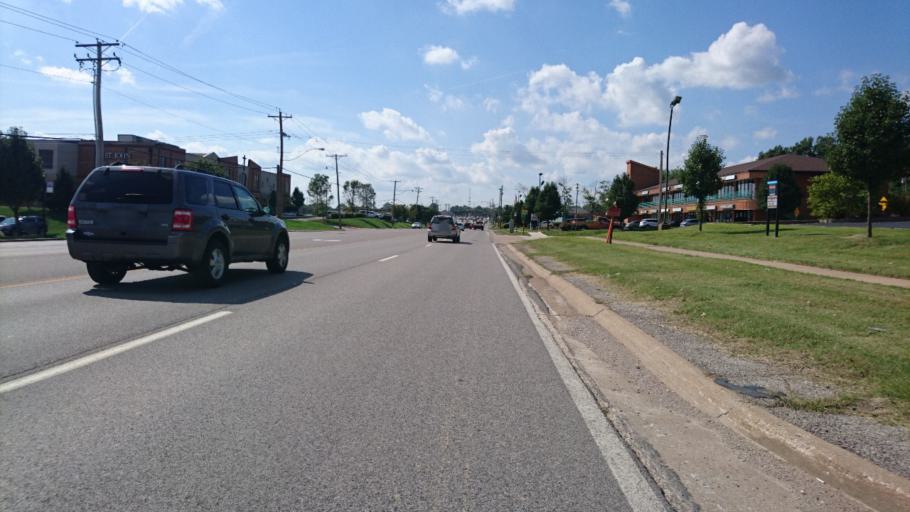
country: US
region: Missouri
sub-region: Saint Louis County
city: Ellisville
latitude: 38.5928
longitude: -90.5805
